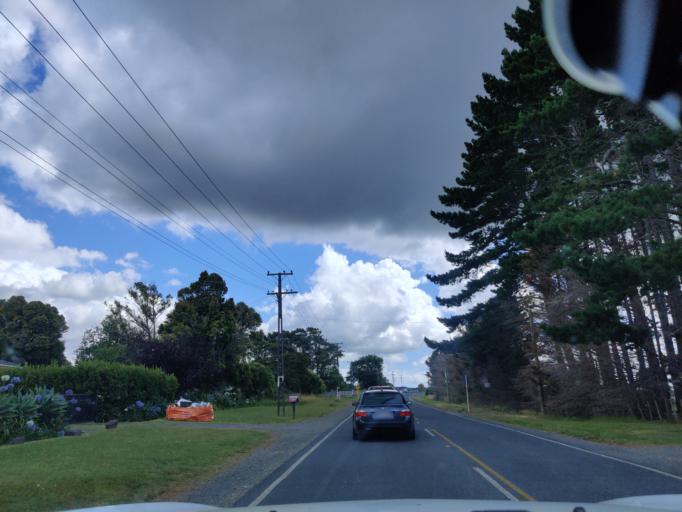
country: NZ
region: Auckland
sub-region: Auckland
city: Red Hill
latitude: -37.0465
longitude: 174.9756
